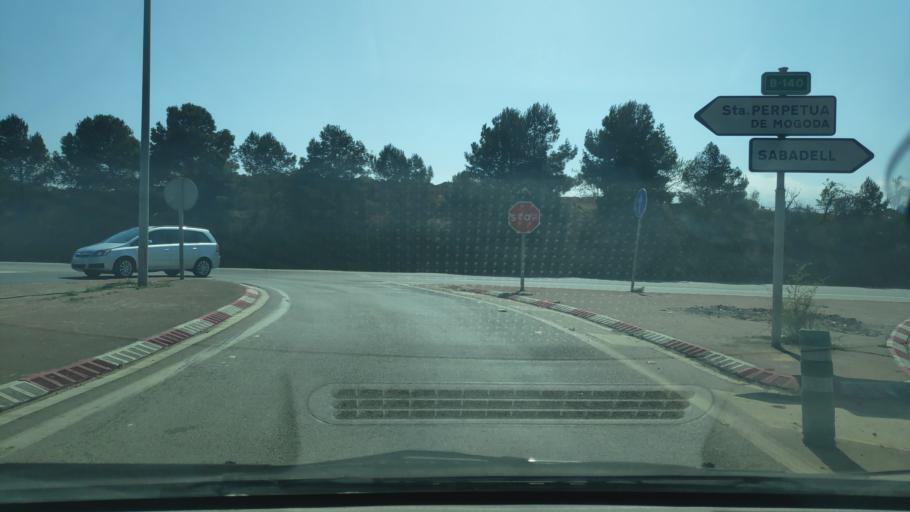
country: ES
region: Catalonia
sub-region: Provincia de Barcelona
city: Barbera del Valles
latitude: 41.5313
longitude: 2.1341
